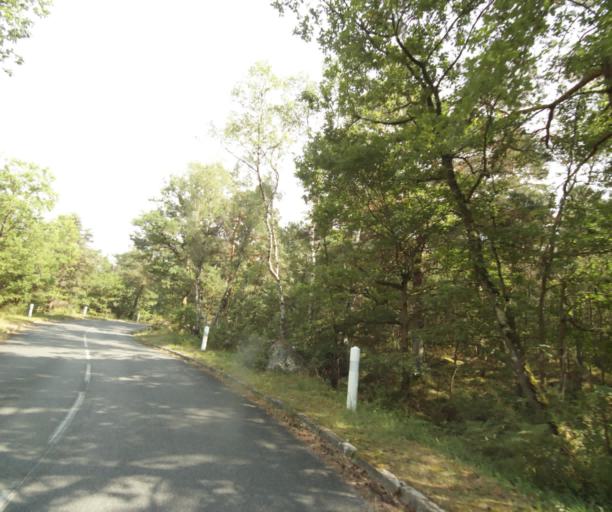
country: FR
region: Ile-de-France
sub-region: Departement de Seine-et-Marne
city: Arbonne-la-Foret
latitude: 48.3850
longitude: 2.5631
